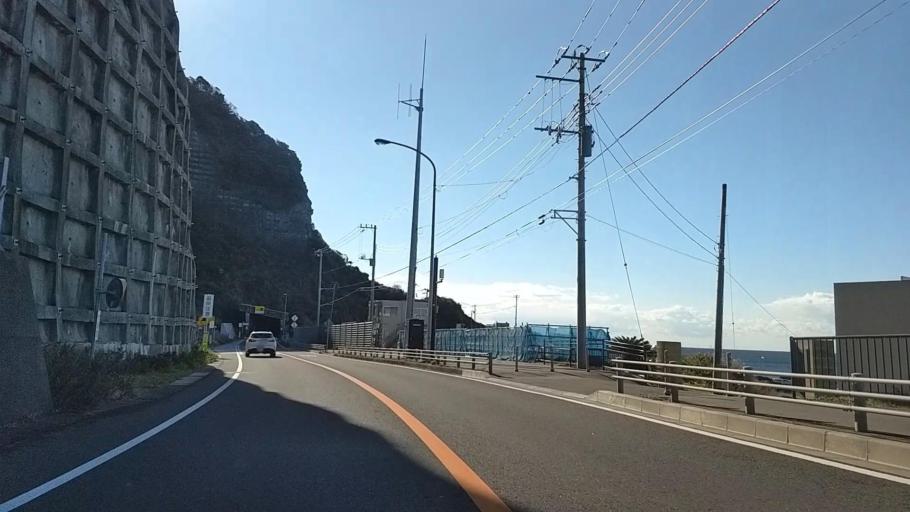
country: JP
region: Chiba
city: Futtsu
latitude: 35.1572
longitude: 139.8191
